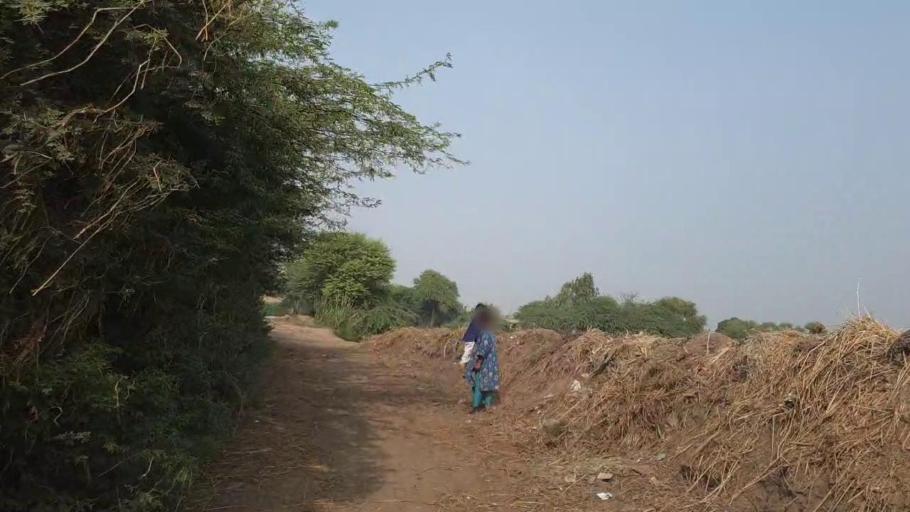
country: PK
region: Sindh
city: Matli
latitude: 25.0288
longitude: 68.5964
